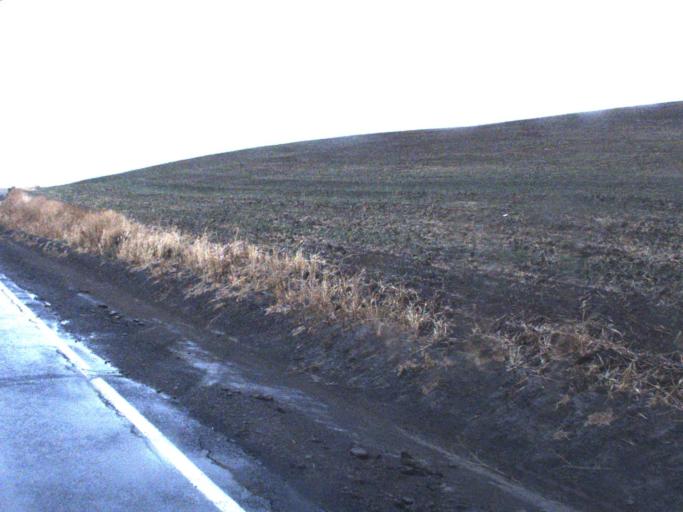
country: US
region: Washington
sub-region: Lincoln County
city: Davenport
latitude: 47.4328
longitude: -118.1881
